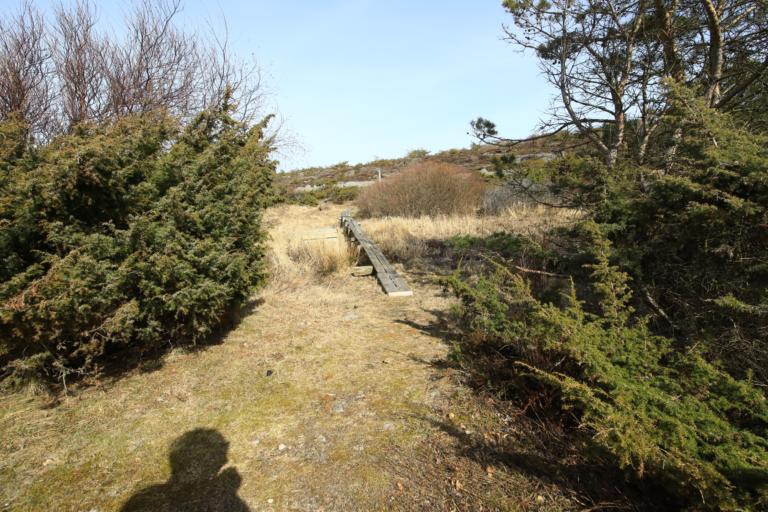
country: SE
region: Halland
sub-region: Kungsbacka Kommun
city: Frillesas
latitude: 57.2676
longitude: 12.1090
